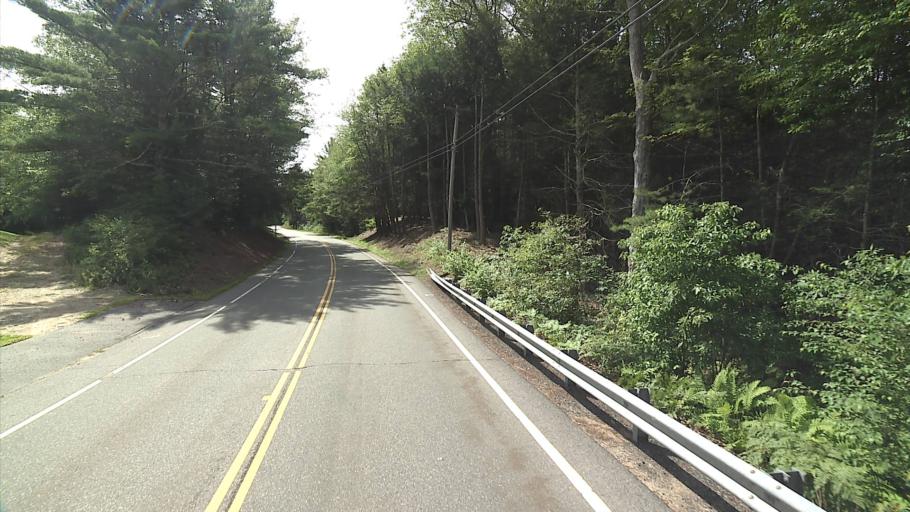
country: US
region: Massachusetts
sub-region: Hampden County
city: Holland
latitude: 41.9489
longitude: -72.1054
